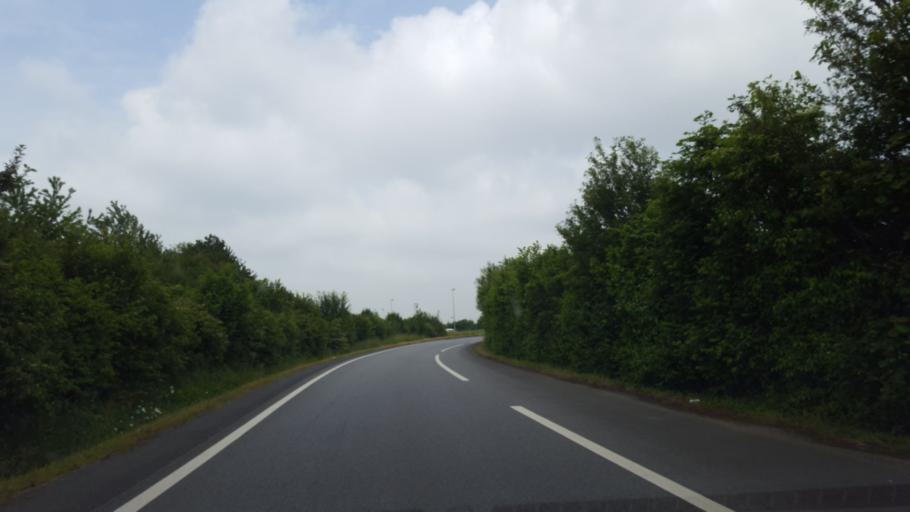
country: FR
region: Brittany
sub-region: Departement d'Ille-et-Vilaine
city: Chartres-de-Bretagne
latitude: 48.0483
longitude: -1.7059
